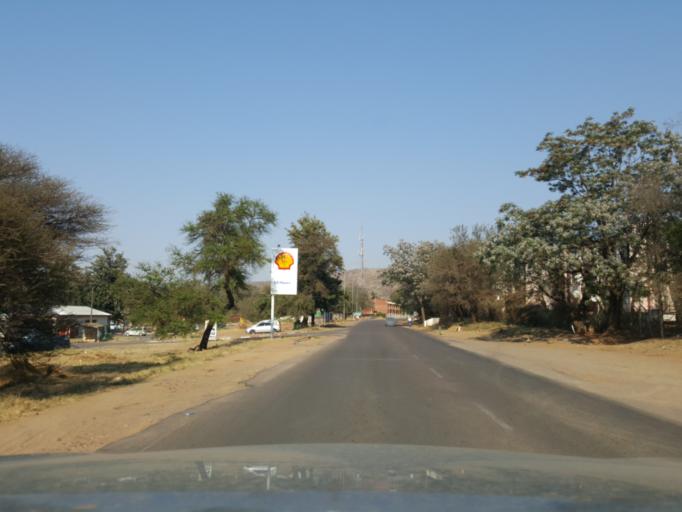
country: BW
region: South East
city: Lobatse
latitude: -25.2280
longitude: 25.6738
